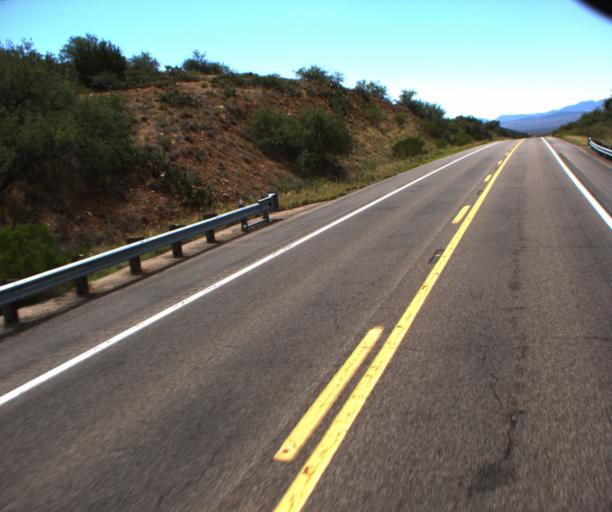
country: US
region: Arizona
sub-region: Gila County
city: Globe
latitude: 33.4672
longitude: -110.7217
